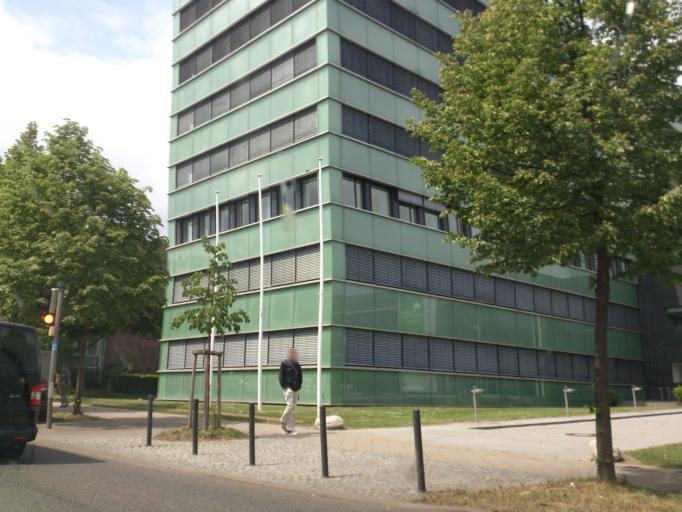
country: DE
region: Hesse
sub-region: Regierungsbezirk Kassel
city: Vellmar
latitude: 51.3141
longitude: 9.4345
